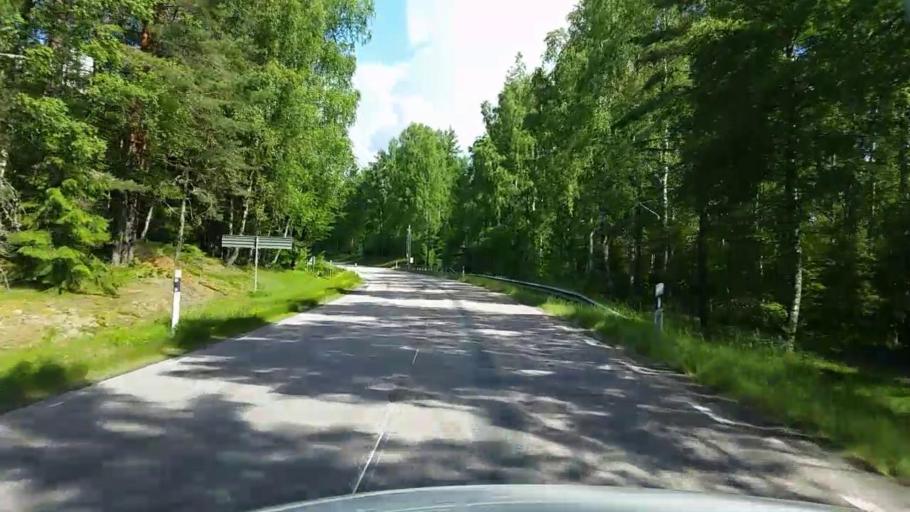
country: SE
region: Vaestmanland
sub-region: Kopings Kommun
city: Kolsva
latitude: 59.6700
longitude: 15.7712
